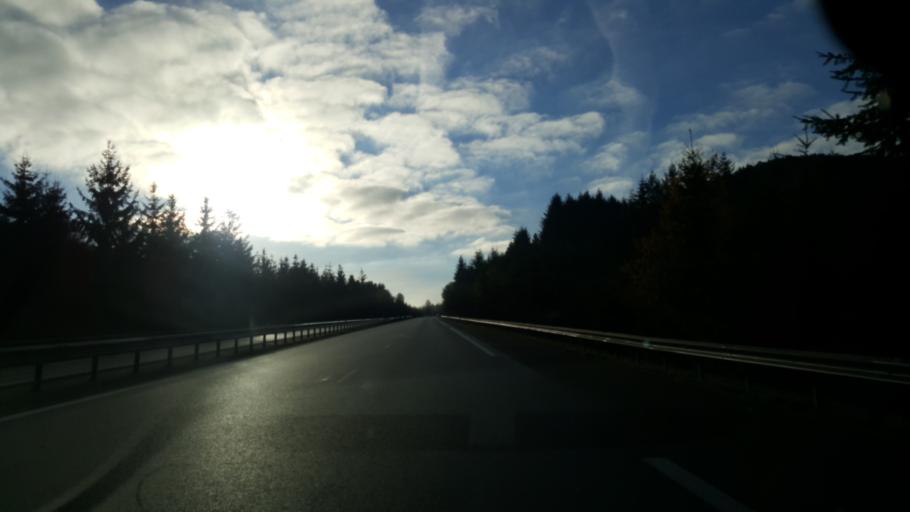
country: FR
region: Auvergne
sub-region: Departement du Puy-de-Dome
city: Chabreloche
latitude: 45.8656
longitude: 3.7172
